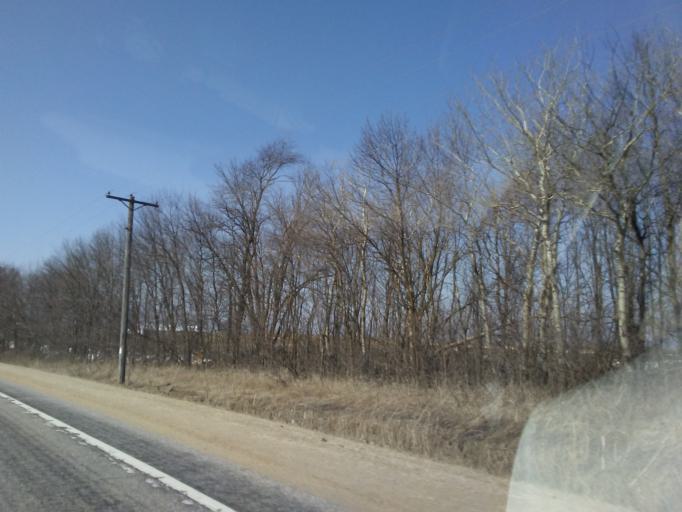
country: US
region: Wisconsin
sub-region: Vernon County
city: Westby
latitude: 43.6678
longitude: -90.8740
